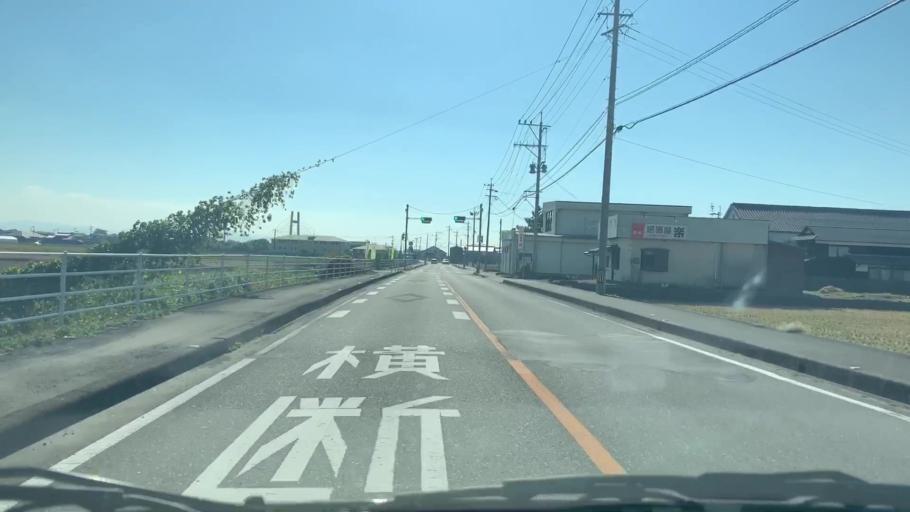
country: JP
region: Saga Prefecture
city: Kanzakimachi-kanzaki
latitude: 33.2931
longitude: 130.4453
